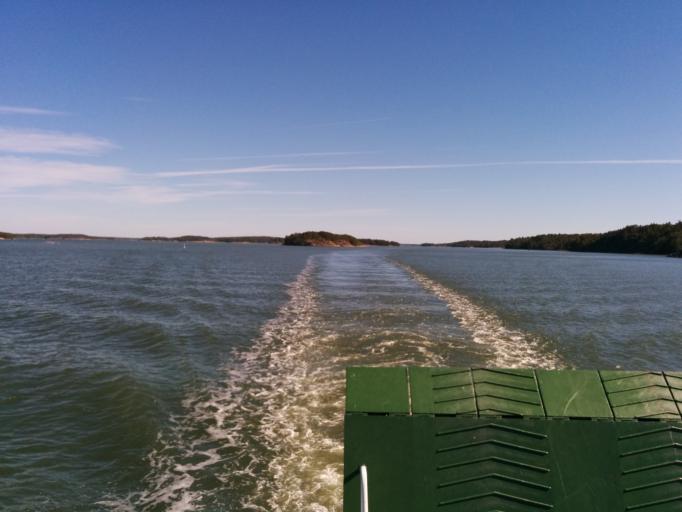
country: FI
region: Varsinais-Suomi
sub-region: Turku
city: Velkua
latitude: 60.4505
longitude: 21.7064
